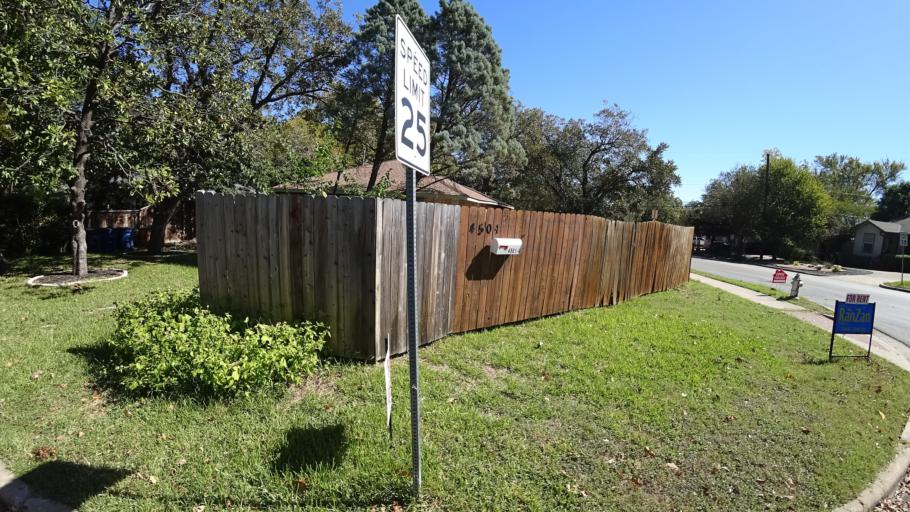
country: US
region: Texas
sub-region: Travis County
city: Austin
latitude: 30.3206
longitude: -97.7524
